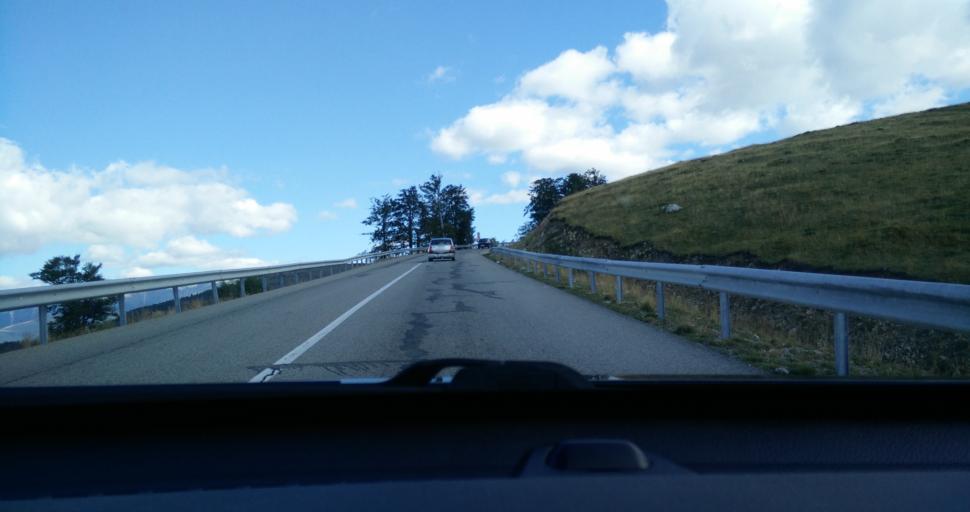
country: RO
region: Gorj
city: Novaci-Straini
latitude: 45.2458
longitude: 23.6936
